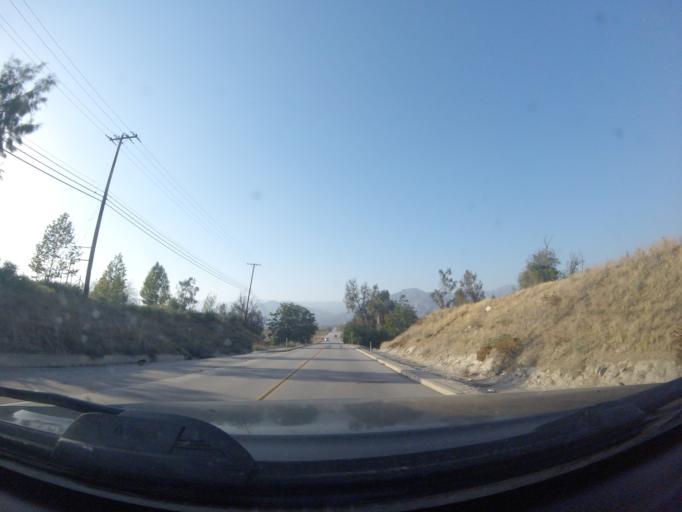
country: US
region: California
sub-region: San Bernardino County
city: Redlands
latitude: 34.0850
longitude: -117.1825
